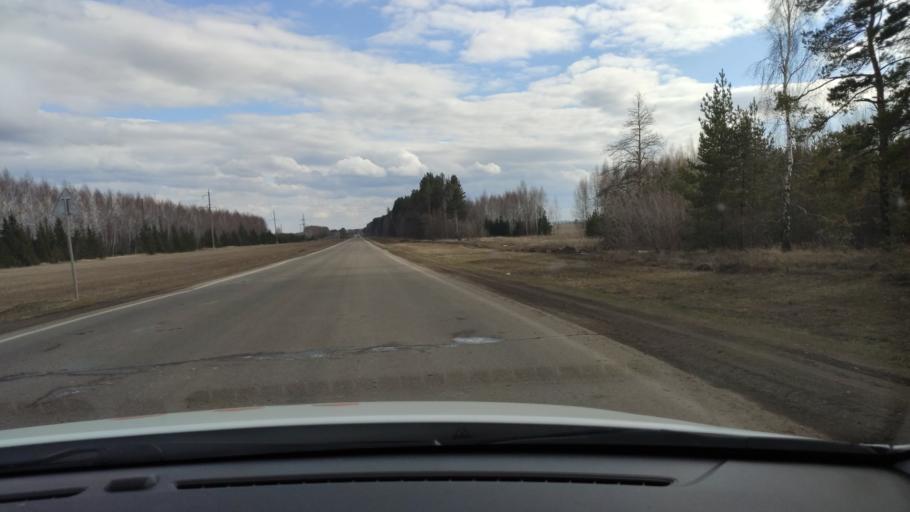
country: RU
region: Tatarstan
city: Vysokaya Gora
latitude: 56.0504
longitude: 49.2135
